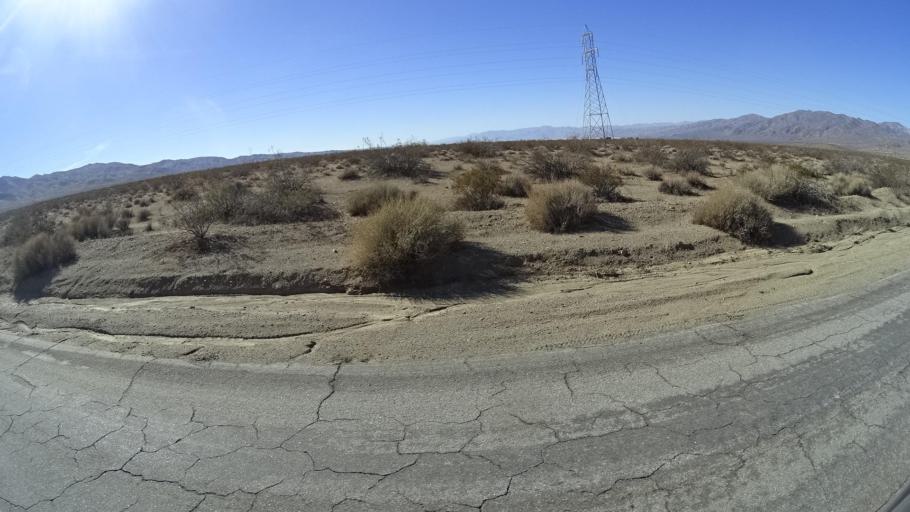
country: US
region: California
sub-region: Kern County
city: Ridgecrest
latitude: 35.4036
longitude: -117.6786
